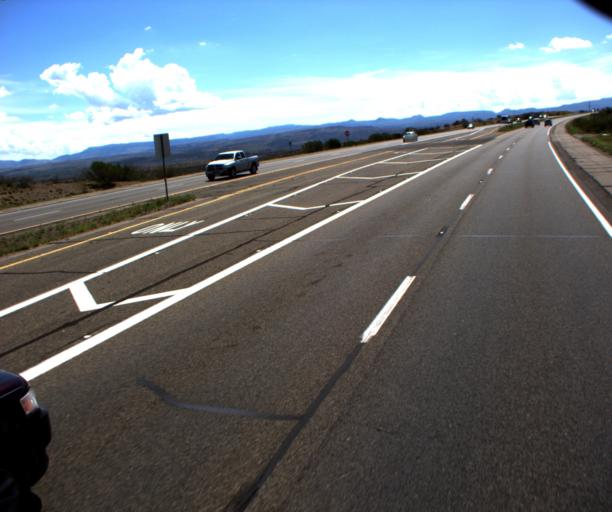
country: US
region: Arizona
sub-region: Yavapai County
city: Spring Valley
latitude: 34.3459
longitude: -112.1438
